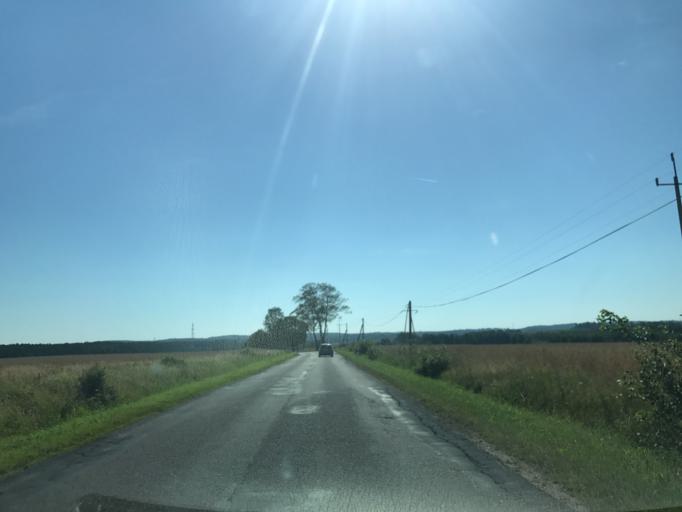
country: PL
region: Pomeranian Voivodeship
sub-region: Powiat bytowski
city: Czarna Dabrowka
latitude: 54.3628
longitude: 17.5210
